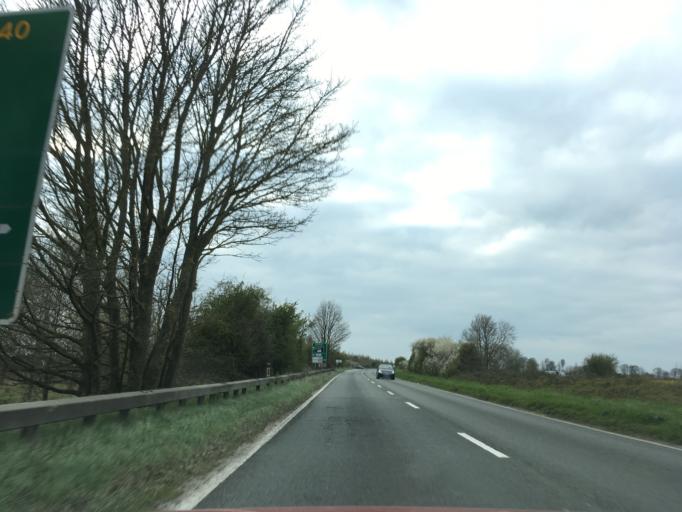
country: GB
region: England
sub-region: Oxfordshire
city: Burford
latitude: 51.8072
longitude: -1.6590
